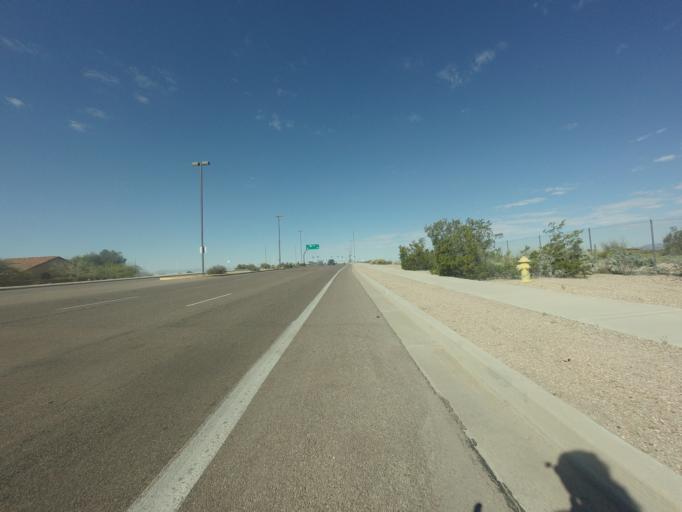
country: US
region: Arizona
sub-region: Pinal County
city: Apache Junction
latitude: 33.4664
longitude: -111.6765
